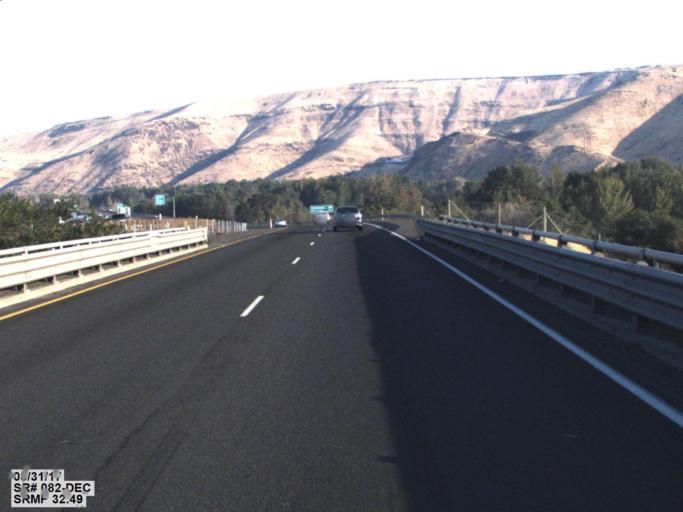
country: US
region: Washington
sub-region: Yakima County
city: Yakima
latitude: 46.6150
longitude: -120.4917
